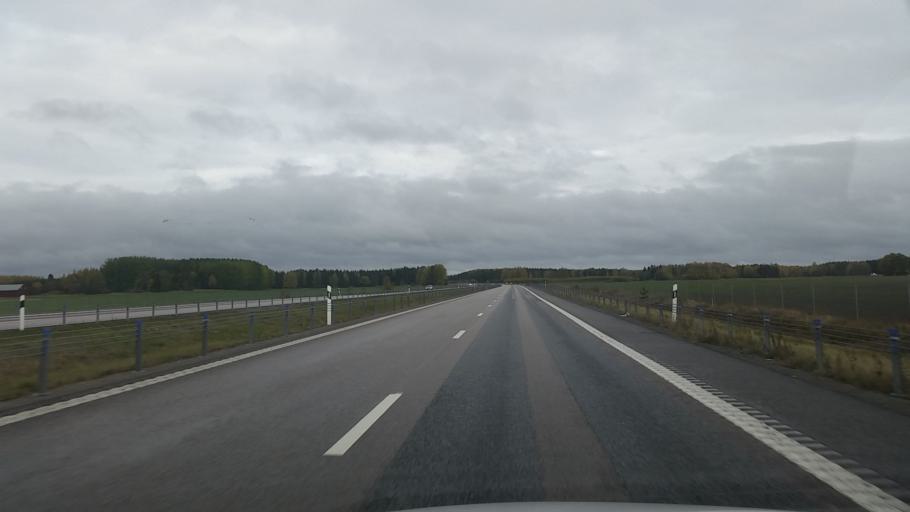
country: SE
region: Uppsala
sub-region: Osthammars Kommun
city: Bjorklinge
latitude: 60.0656
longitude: 17.6105
